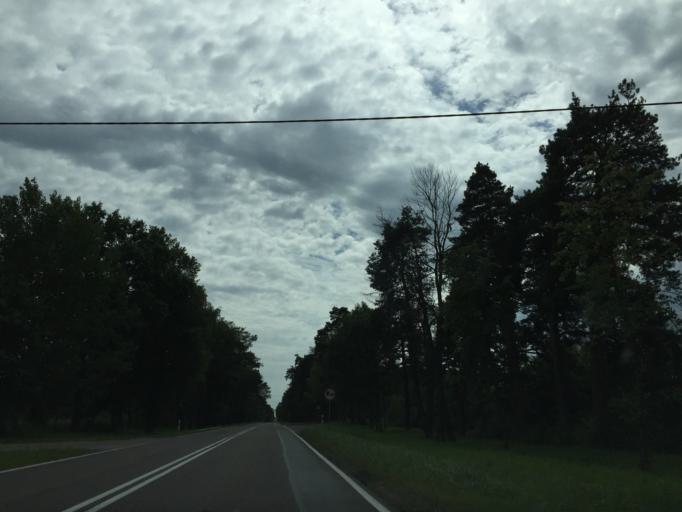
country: PL
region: Podlasie
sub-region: Powiat bielski
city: Bielsk Podlaski
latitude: 52.7160
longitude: 23.1401
